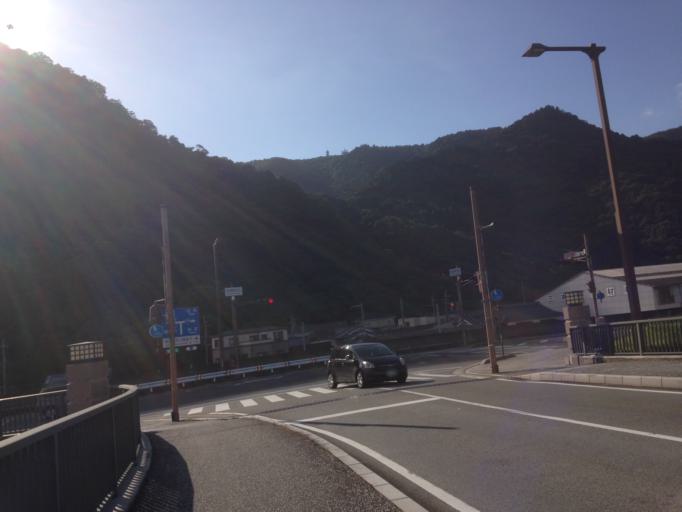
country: JP
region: Hyogo
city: Tatsunocho-tominaga
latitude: 34.8746
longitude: 134.5486
